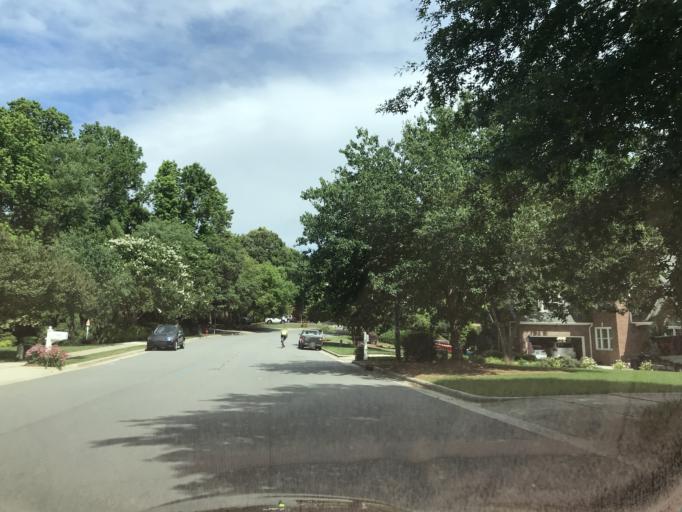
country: US
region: North Carolina
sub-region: Wake County
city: West Raleigh
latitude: 35.8832
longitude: -78.6855
